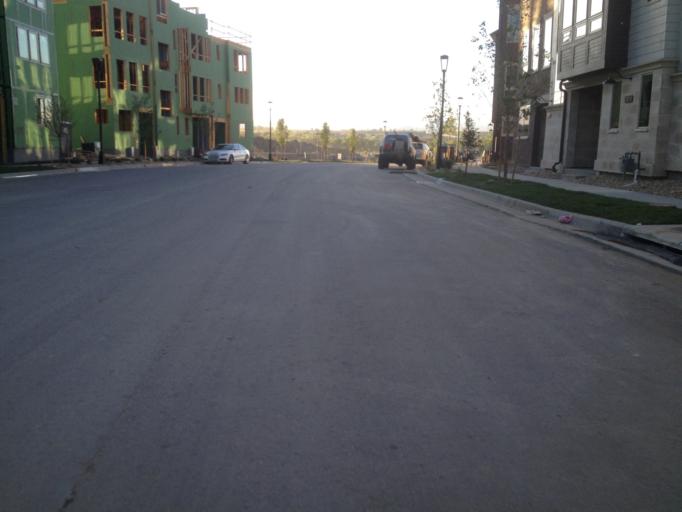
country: US
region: Colorado
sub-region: Boulder County
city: Superior
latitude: 39.9496
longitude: -105.1596
